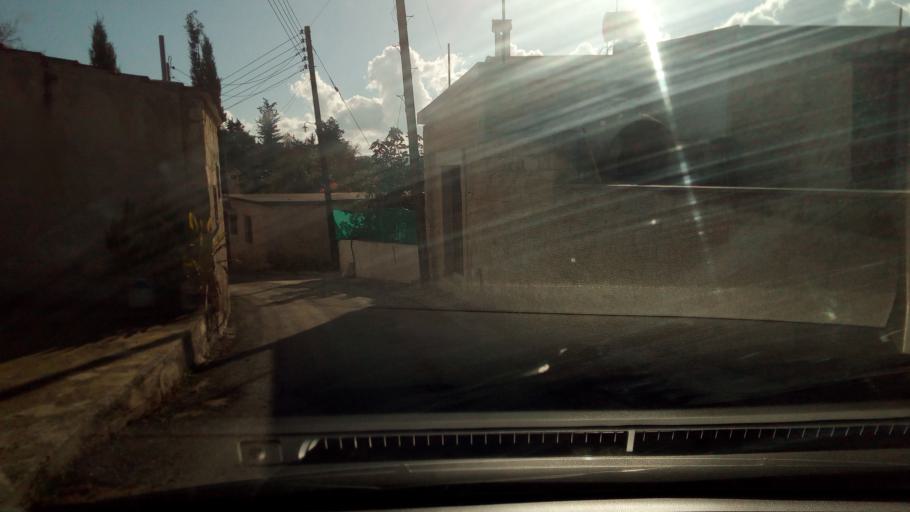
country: CY
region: Pafos
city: Polis
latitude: 34.9413
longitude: 32.5031
